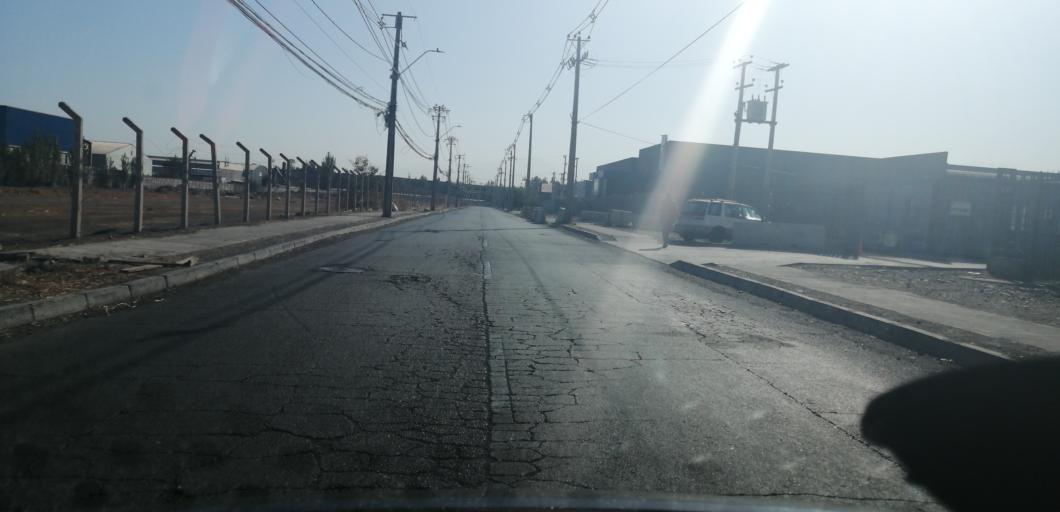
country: CL
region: Santiago Metropolitan
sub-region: Provincia de Santiago
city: Lo Prado
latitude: -33.3808
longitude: -70.7662
